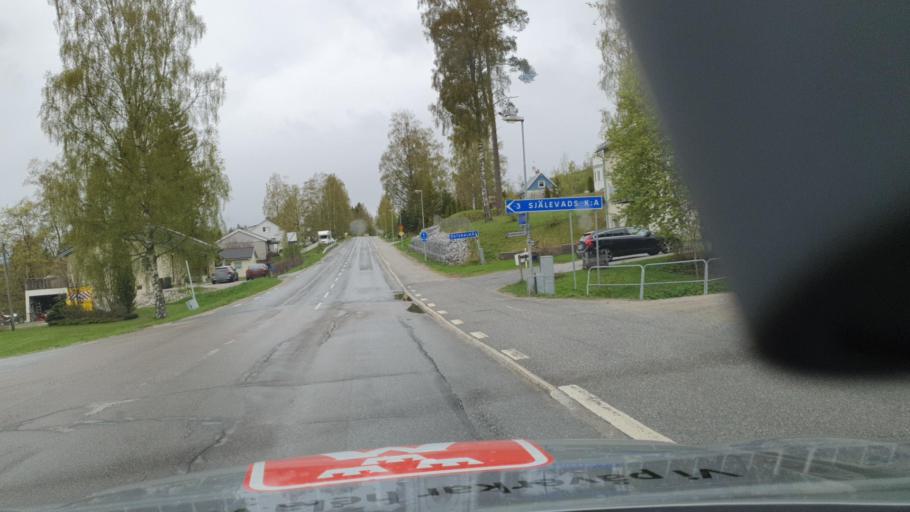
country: SE
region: Vaesternorrland
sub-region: OErnskoeldsviks Kommun
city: Ornskoldsvik
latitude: 63.3036
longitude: 18.5863
